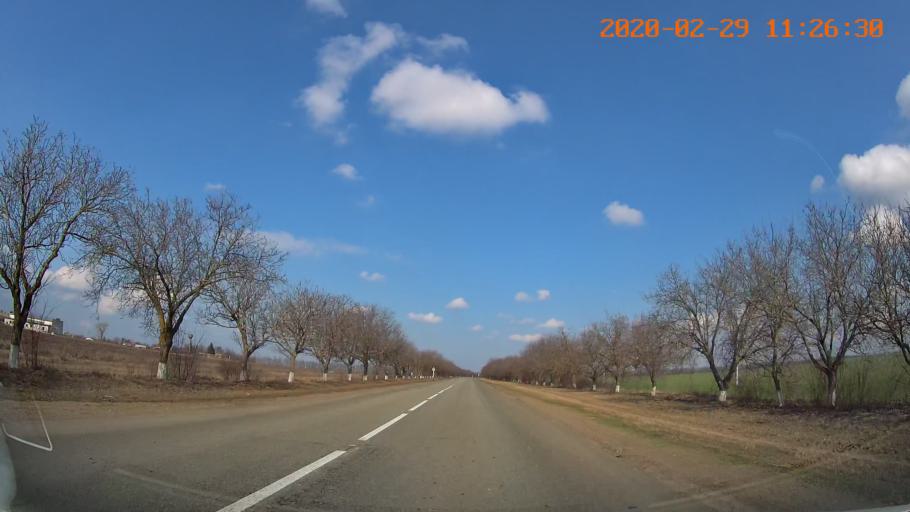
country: MD
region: Telenesti
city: Cocieri
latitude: 47.4539
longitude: 29.1458
